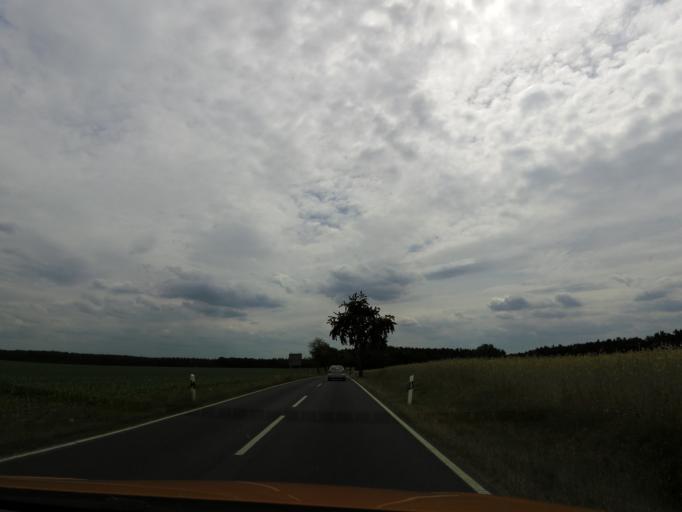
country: DE
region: Brandenburg
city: Rangsdorf
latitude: 52.2417
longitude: 13.3881
